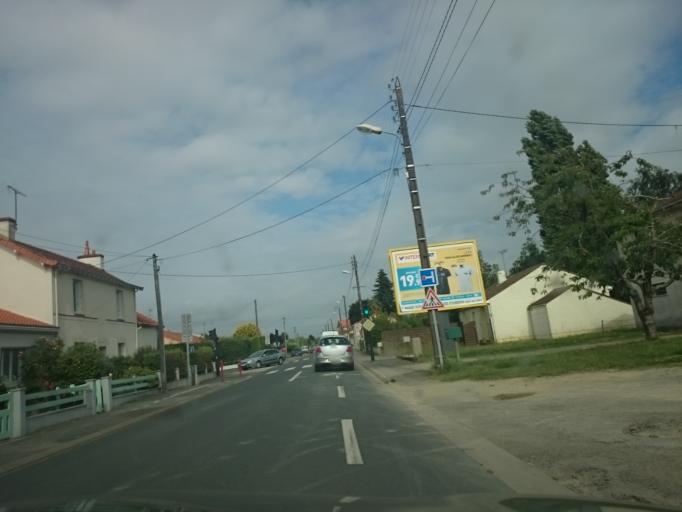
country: FR
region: Pays de la Loire
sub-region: Departement de la Loire-Atlantique
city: Le Pellerin
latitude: 47.2003
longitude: -1.7661
